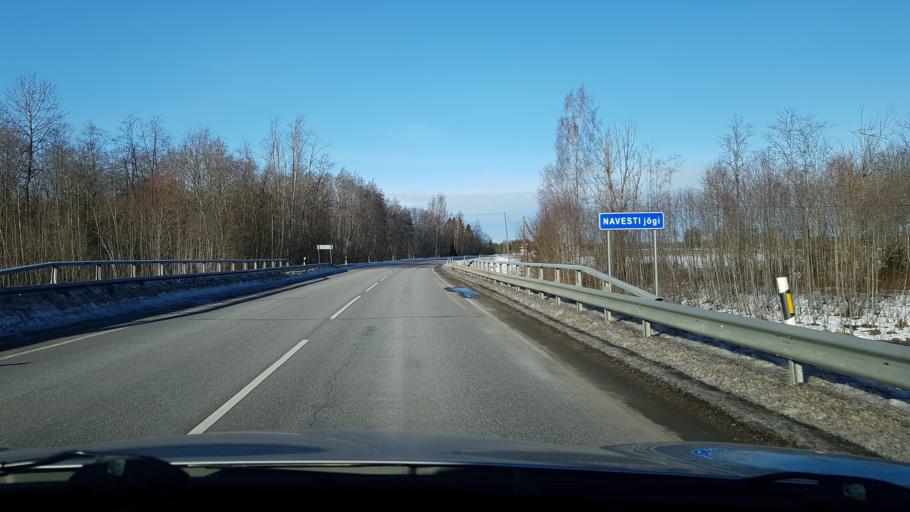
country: EE
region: Jogevamaa
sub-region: Poltsamaa linn
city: Poltsamaa
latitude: 58.6311
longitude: 25.7803
